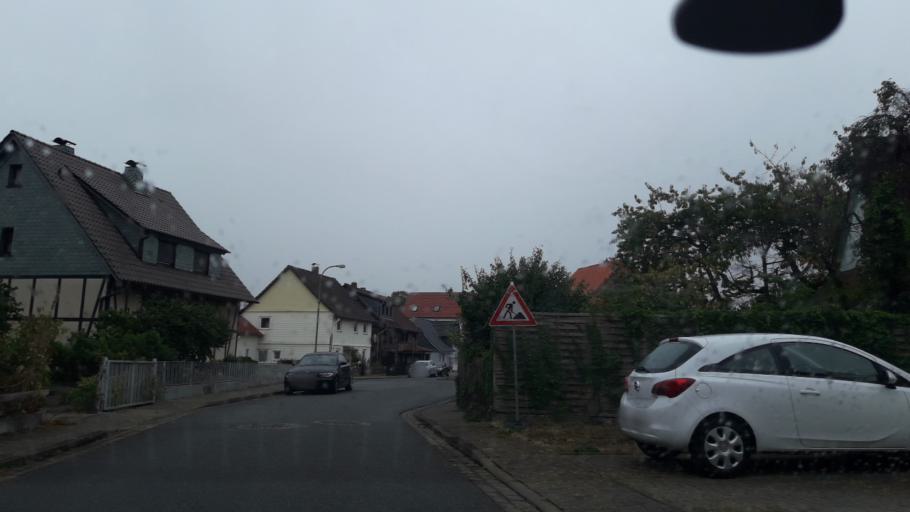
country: DE
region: Lower Saxony
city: Vienenburg
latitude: 51.9621
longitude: 10.5886
